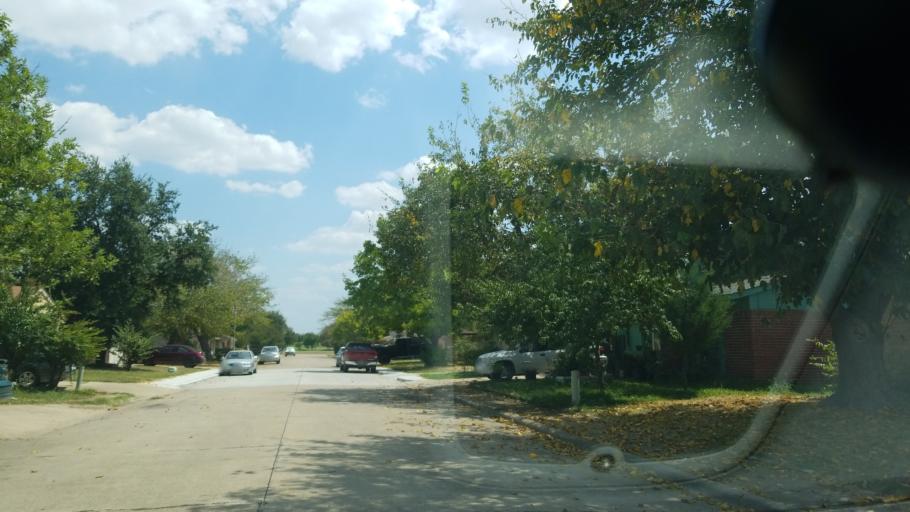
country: US
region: Texas
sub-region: Dallas County
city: Grand Prairie
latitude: 32.6992
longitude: -96.9885
